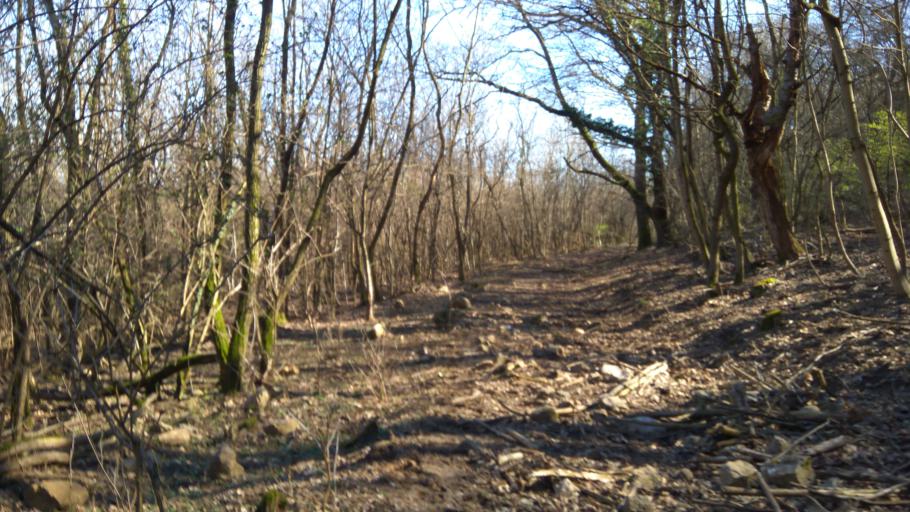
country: HU
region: Pest
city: Csobanka
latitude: 47.6343
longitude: 18.9836
